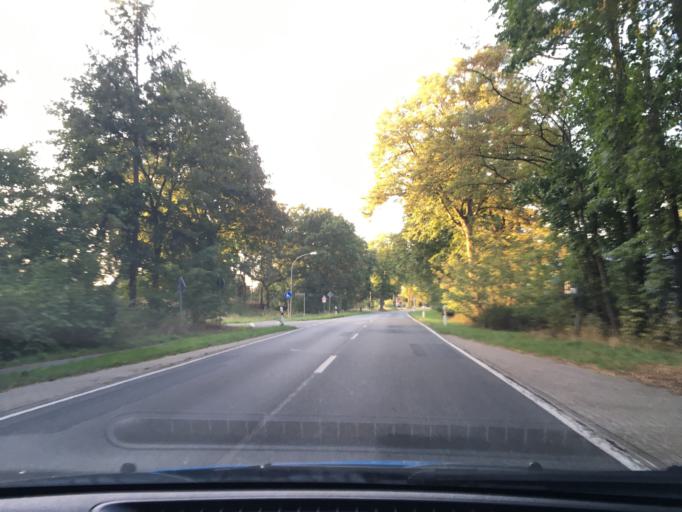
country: DE
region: Lower Saxony
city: Bleckede
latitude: 53.2789
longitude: 10.7413
